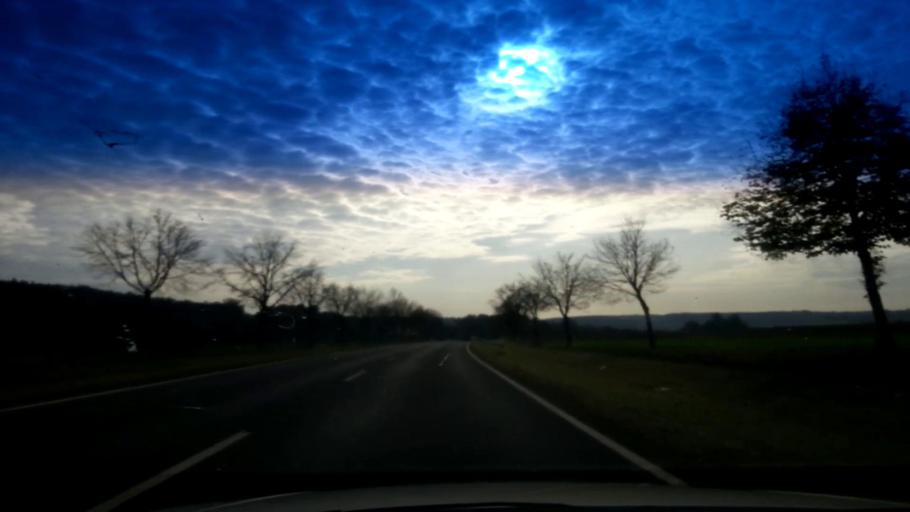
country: DE
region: Bavaria
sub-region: Upper Franconia
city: Stegaurach
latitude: 49.8625
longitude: 10.8818
